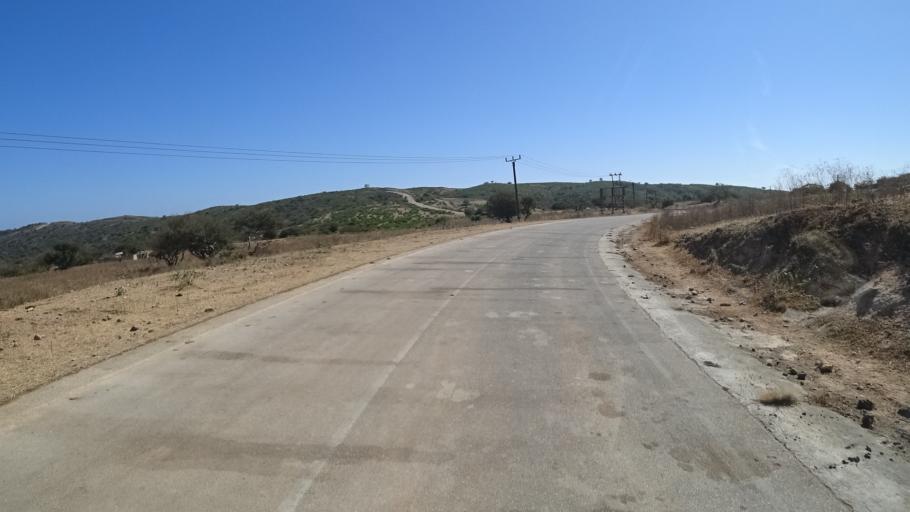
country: YE
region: Al Mahrah
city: Hawf
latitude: 16.7557
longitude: 53.3408
